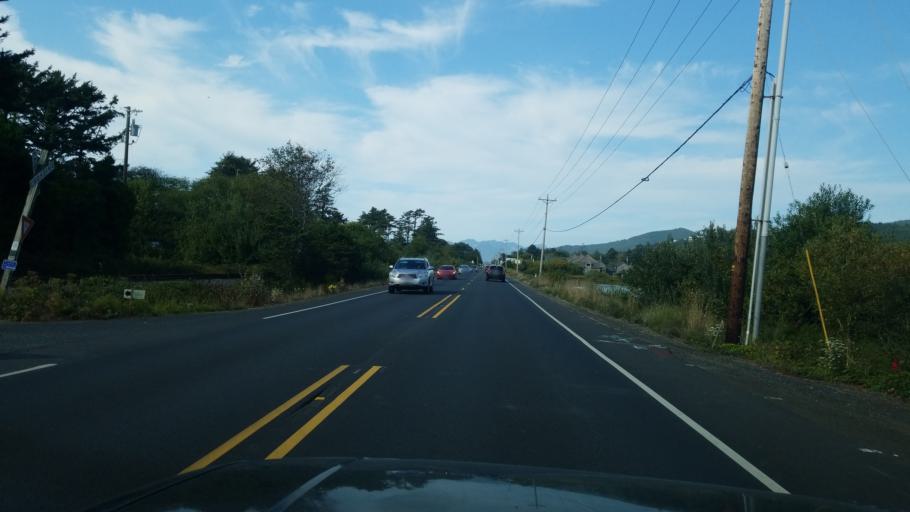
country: US
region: Oregon
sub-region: Tillamook County
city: Rockaway Beach
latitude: 45.5924
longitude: -123.9475
